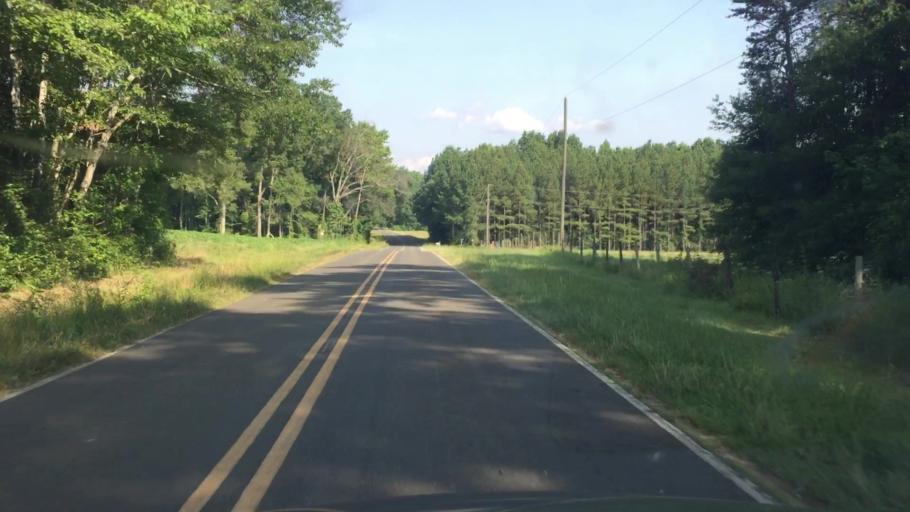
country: US
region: North Carolina
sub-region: Rockingham County
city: Reidsville
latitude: 36.2792
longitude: -79.5920
